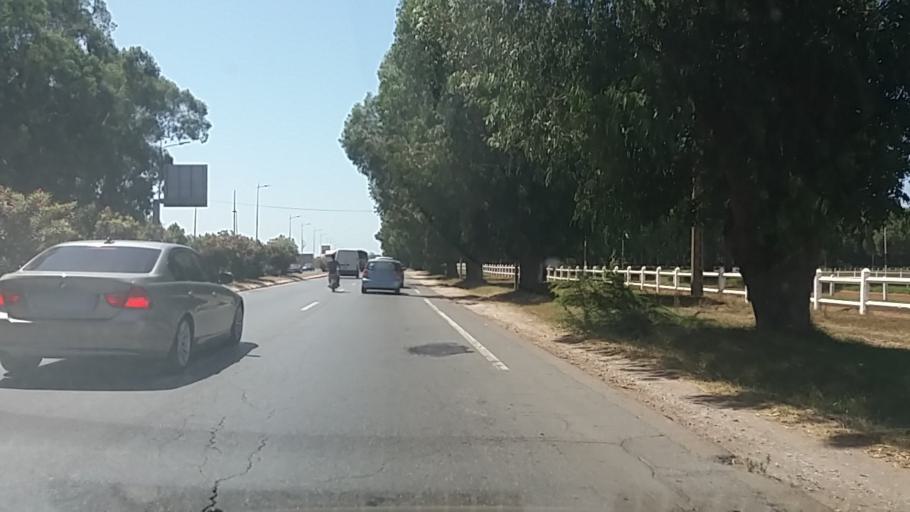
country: MA
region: Rabat-Sale-Zemmour-Zaer
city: Sale
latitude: 34.0289
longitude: -6.7335
